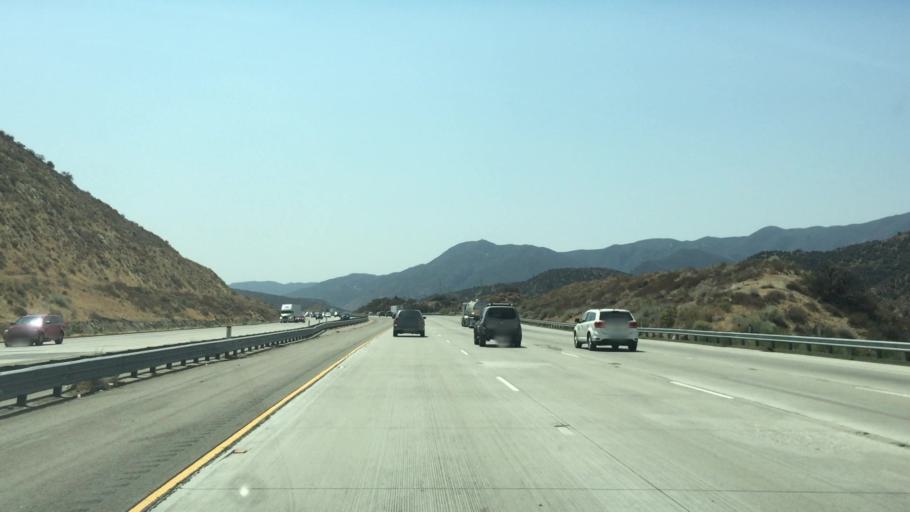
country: US
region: California
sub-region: Kern County
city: Lebec
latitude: 34.7003
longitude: -118.7931
